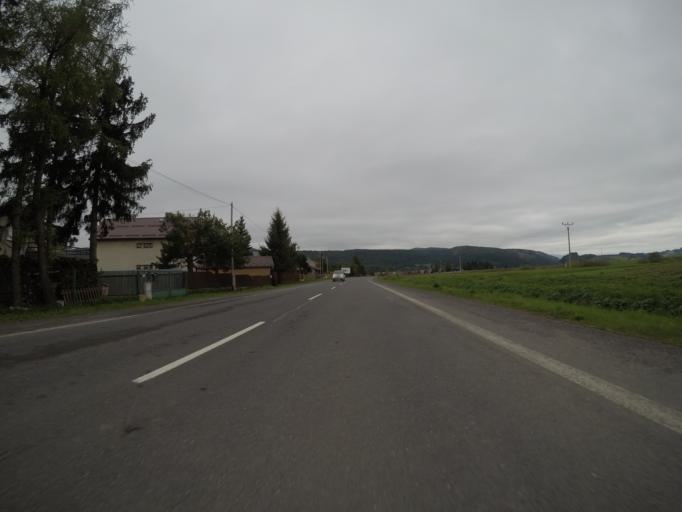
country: SK
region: Presovsky
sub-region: Okres Poprad
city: Strba
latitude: 49.0643
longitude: 19.9827
